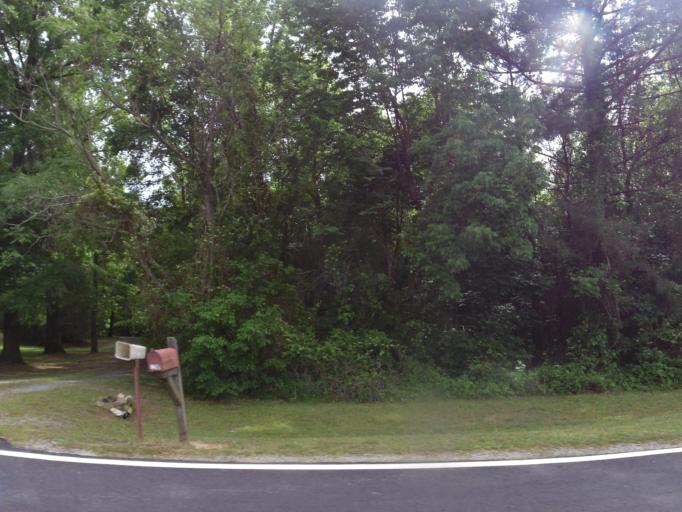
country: US
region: Georgia
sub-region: McDuffie County
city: Thomson
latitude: 33.5366
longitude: -82.4967
